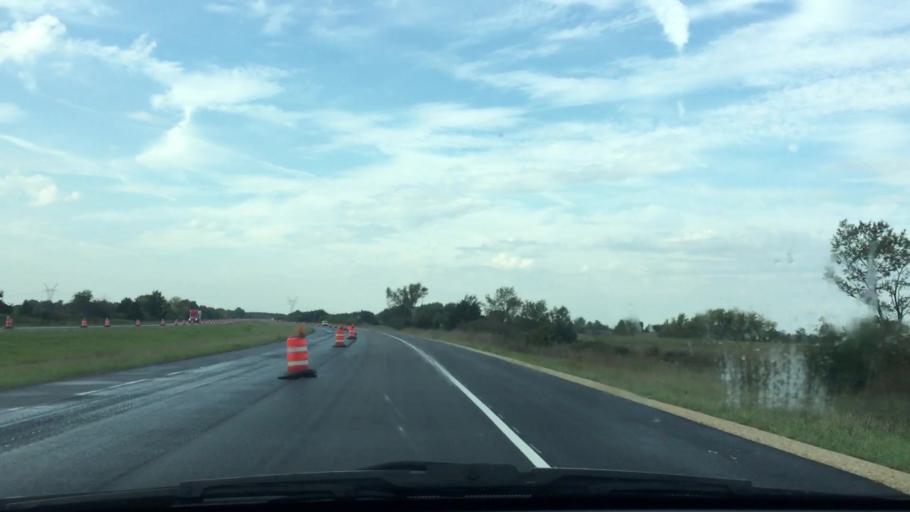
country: US
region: Illinois
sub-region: Whiteside County
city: Erie
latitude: 41.7042
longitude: -90.0566
